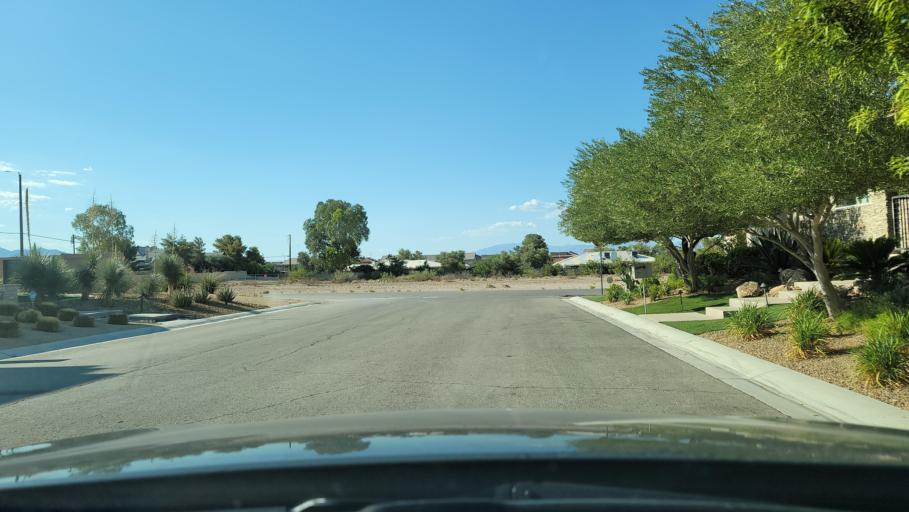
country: US
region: Nevada
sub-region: Clark County
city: Spring Valley
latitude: 36.0831
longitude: -115.2324
